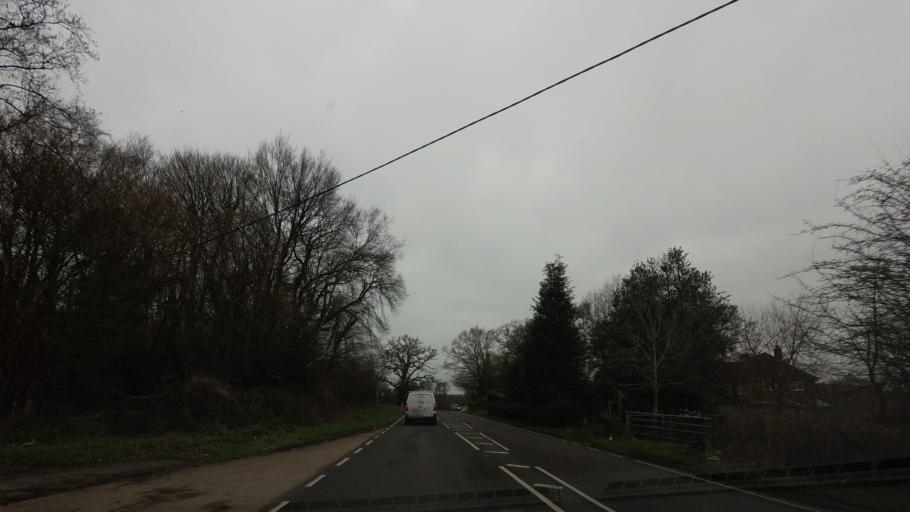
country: GB
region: England
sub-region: East Sussex
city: Battle
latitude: 50.9296
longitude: 0.5264
